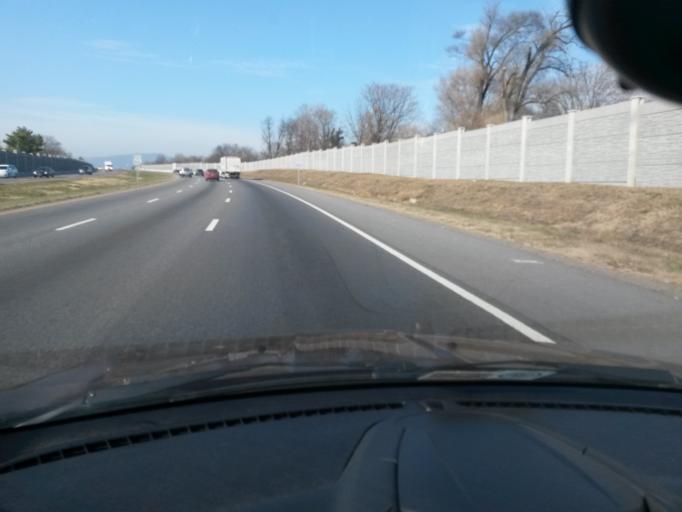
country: US
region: Virginia
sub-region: City of Roanoke
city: Roanoke
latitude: 37.2914
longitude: -79.9424
